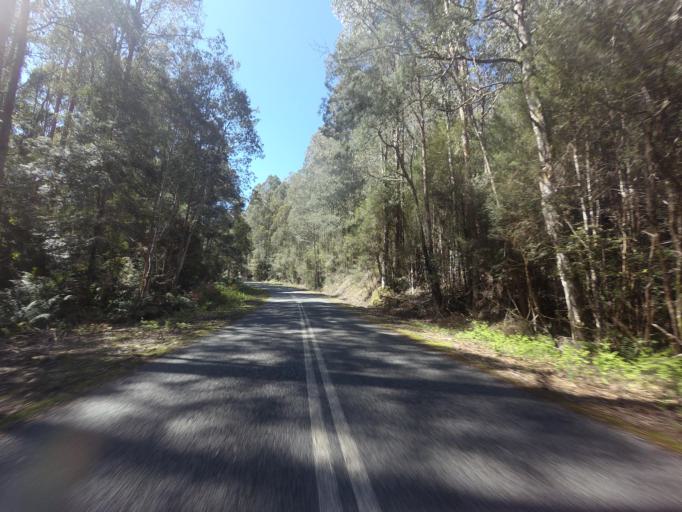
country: AU
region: Tasmania
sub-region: Huon Valley
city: Geeveston
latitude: -42.7868
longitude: 146.3988
